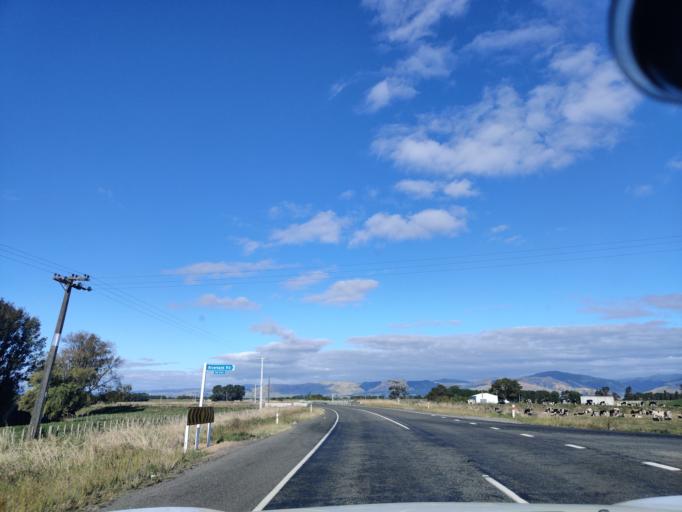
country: NZ
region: Manawatu-Wanganui
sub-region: Horowhenua District
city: Foxton
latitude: -40.4251
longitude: 175.4531
